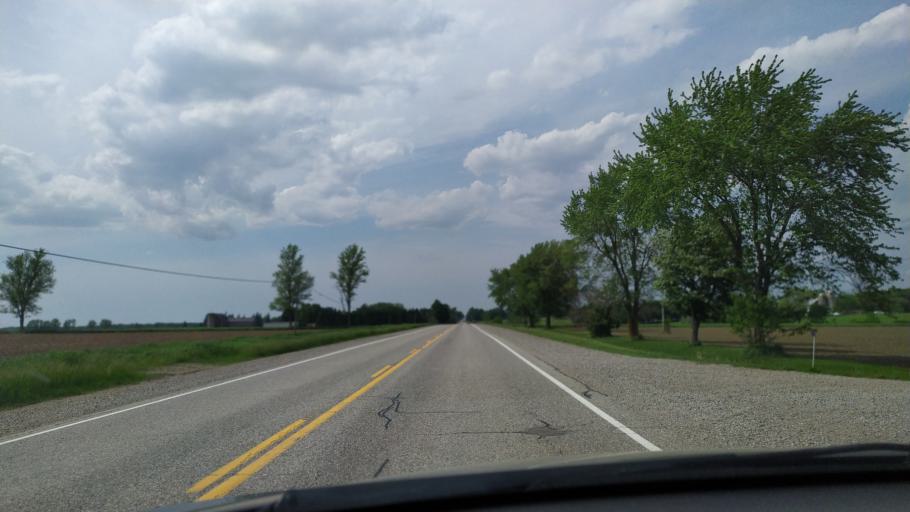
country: CA
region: Ontario
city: Dorchester
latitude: 43.1269
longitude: -81.0240
